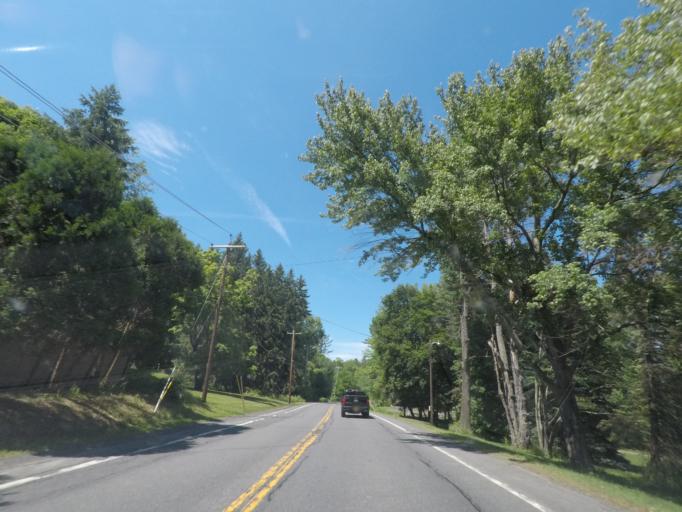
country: US
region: Massachusetts
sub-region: Berkshire County
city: Great Barrington
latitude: 42.1911
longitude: -73.5124
